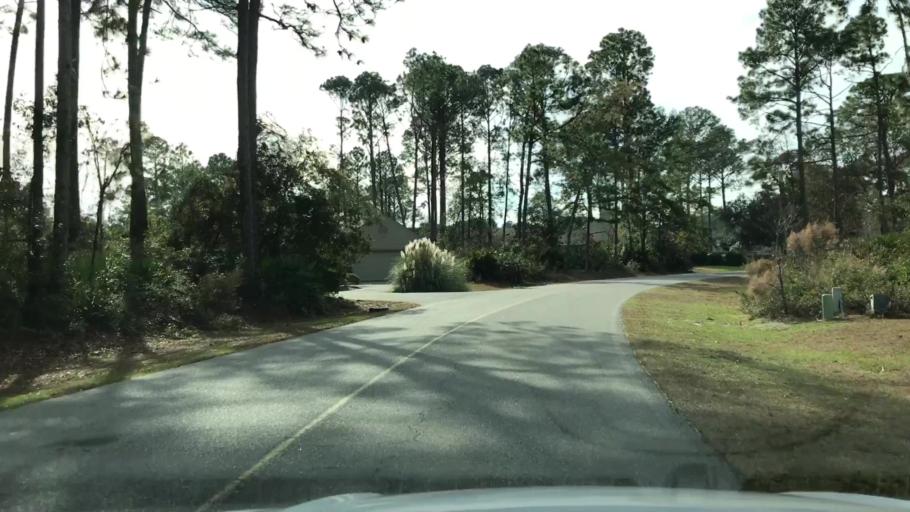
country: US
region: South Carolina
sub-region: Beaufort County
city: Hilton Head Island
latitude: 32.2403
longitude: -80.7090
